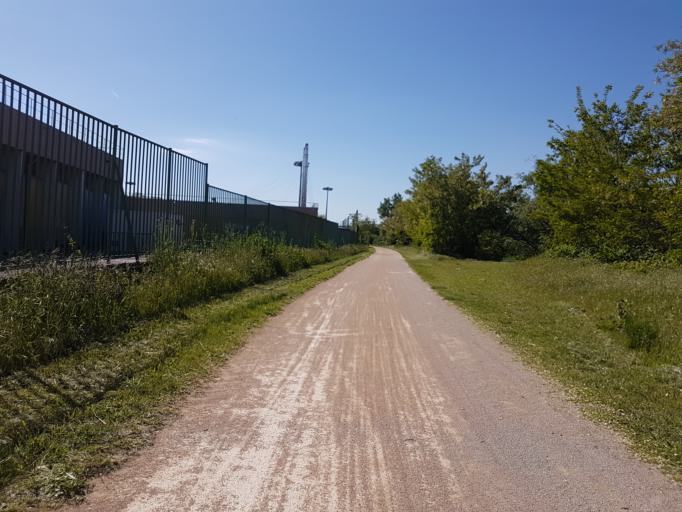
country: FR
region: Rhone-Alpes
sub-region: Departement du Rhone
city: Vaulx-en-Velin
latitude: 45.7671
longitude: 4.9100
